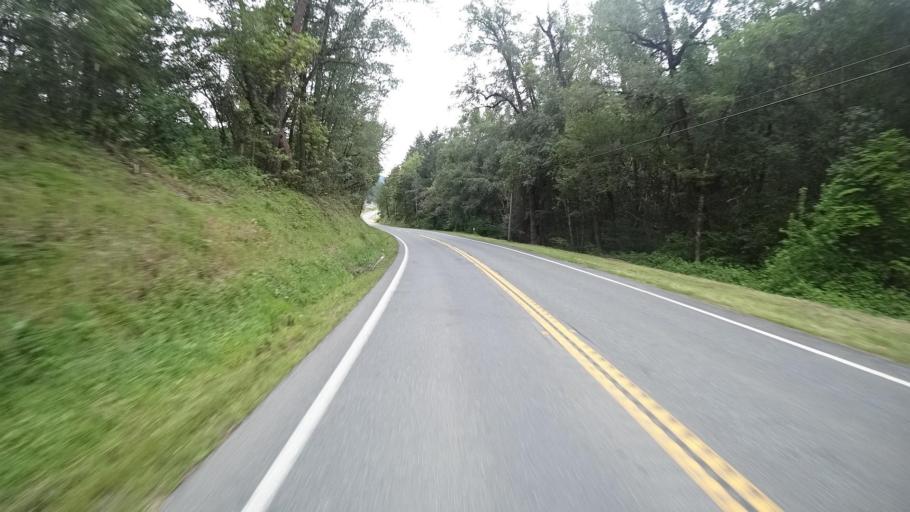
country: US
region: California
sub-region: Humboldt County
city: Willow Creek
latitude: 40.9544
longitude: -123.6431
